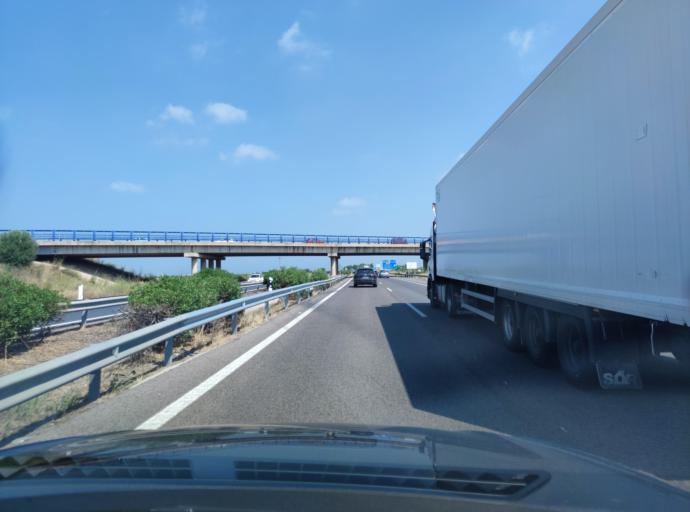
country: ES
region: Valencia
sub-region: Provincia de Castello
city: Alquerias del Nino Perdido
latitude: 39.8871
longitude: -0.1273
